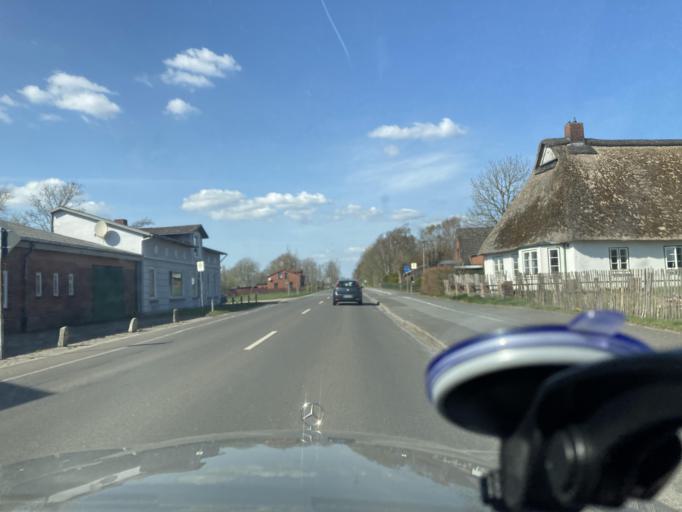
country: DE
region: Schleswig-Holstein
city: Krempel
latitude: 54.2993
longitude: 9.0384
